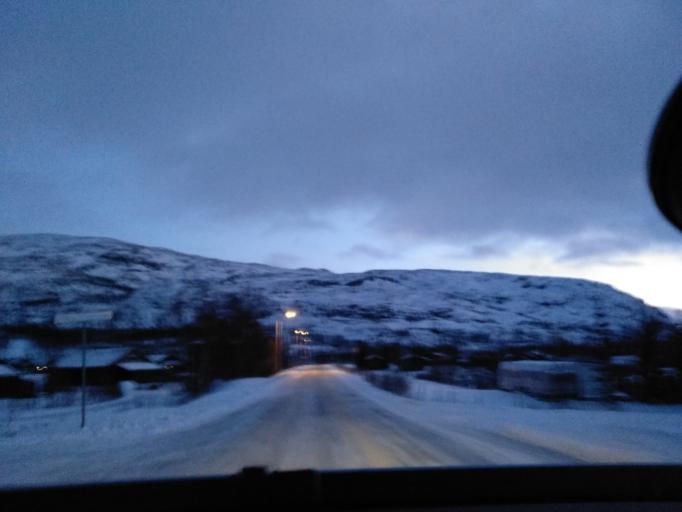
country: NO
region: Vest-Agder
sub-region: Sirdal
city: Tonstad
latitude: 59.0157
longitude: 6.9375
